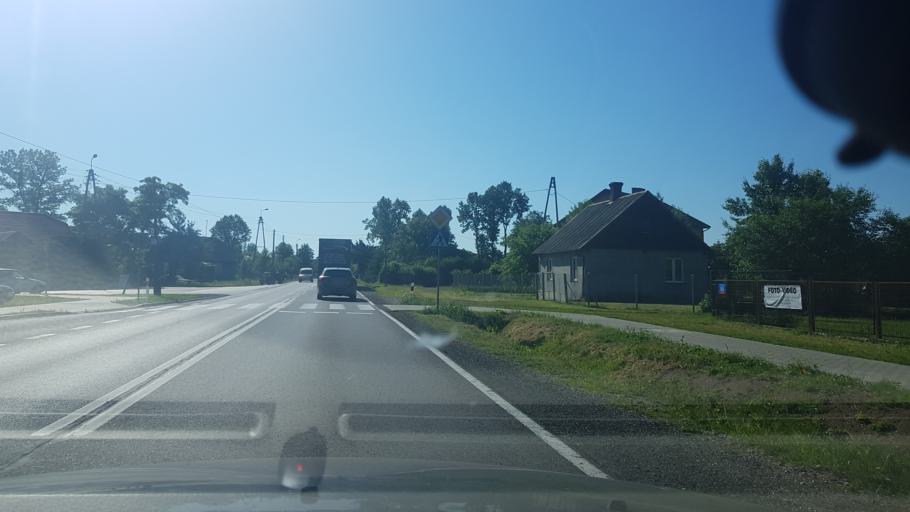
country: PL
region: Masovian Voivodeship
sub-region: Powiat wegrowski
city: Lochow
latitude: 52.5486
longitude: 21.6294
